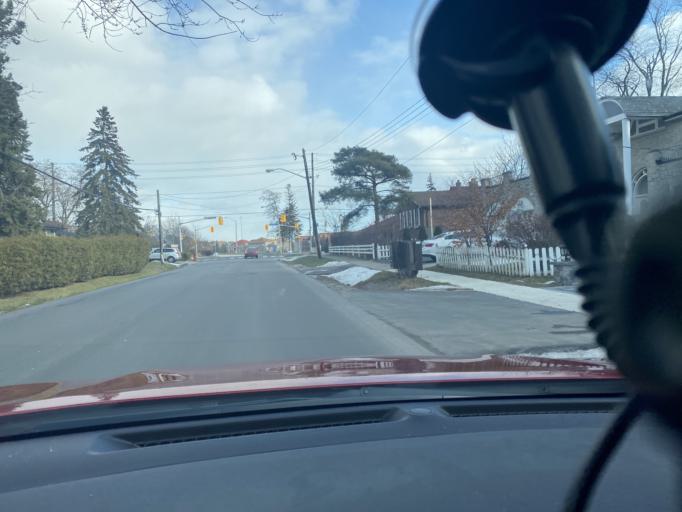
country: CA
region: Ontario
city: Scarborough
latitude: 43.7957
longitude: -79.1661
